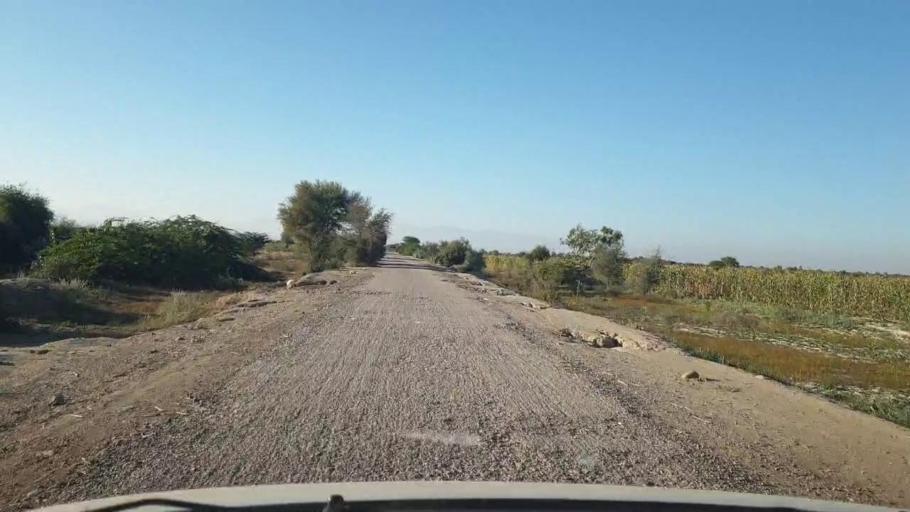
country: PK
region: Sindh
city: Johi
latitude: 26.7665
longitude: 67.4627
